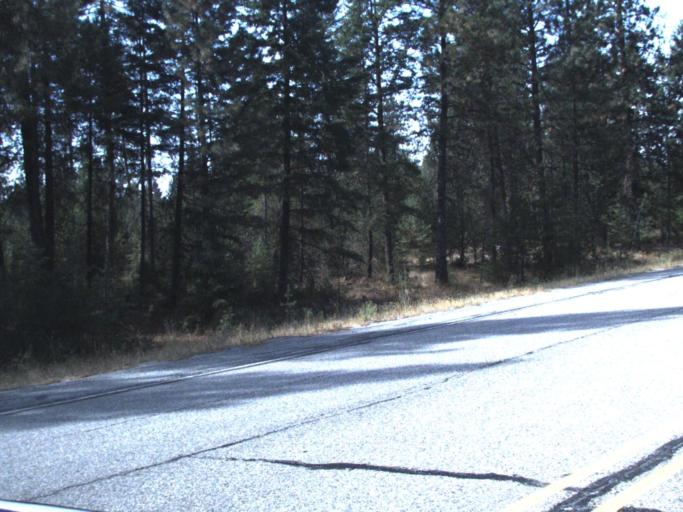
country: US
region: Washington
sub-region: Stevens County
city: Chewelah
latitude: 48.1446
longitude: -117.6725
